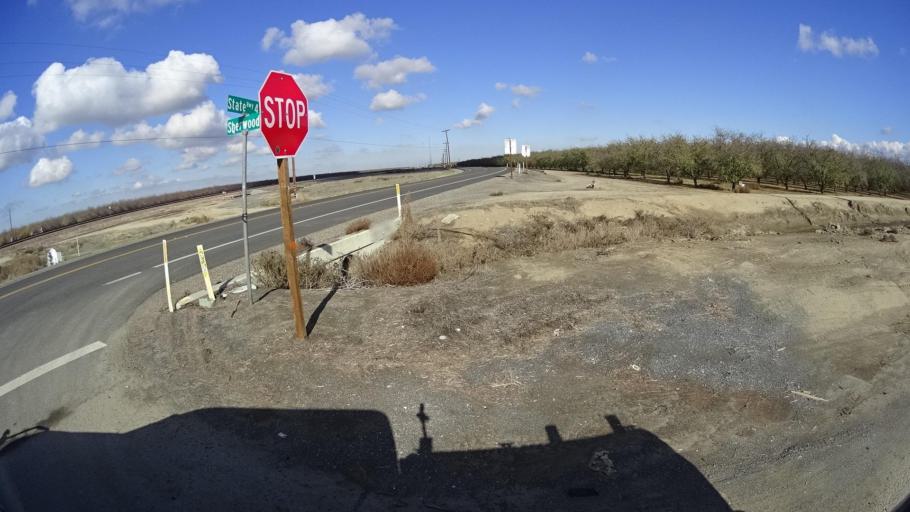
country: US
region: California
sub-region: Kern County
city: Wasco
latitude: 35.6742
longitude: -119.3303
